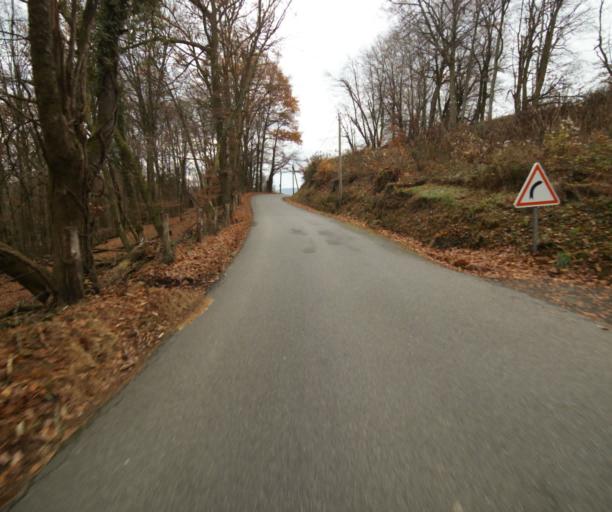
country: FR
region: Limousin
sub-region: Departement de la Correze
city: Tulle
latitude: 45.2569
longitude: 1.7299
